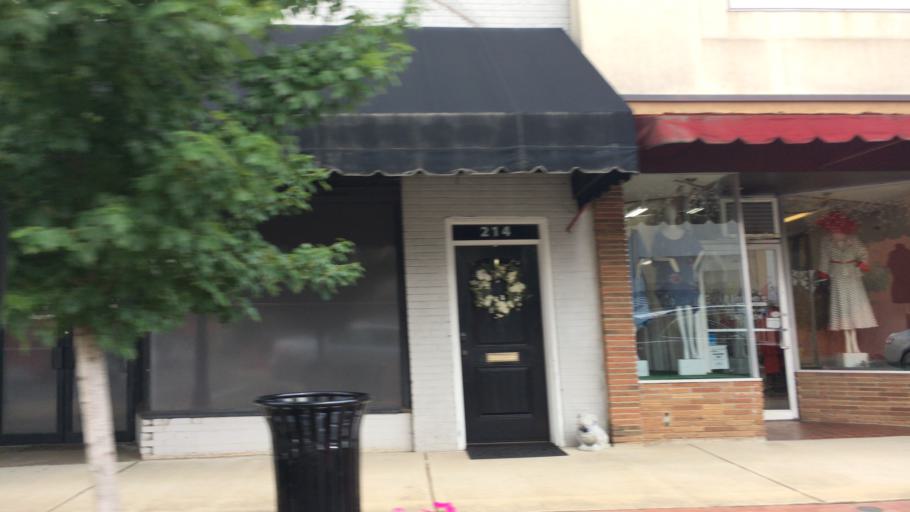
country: US
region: Louisiana
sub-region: Lincoln Parish
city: Ruston
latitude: 32.5305
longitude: -92.6391
